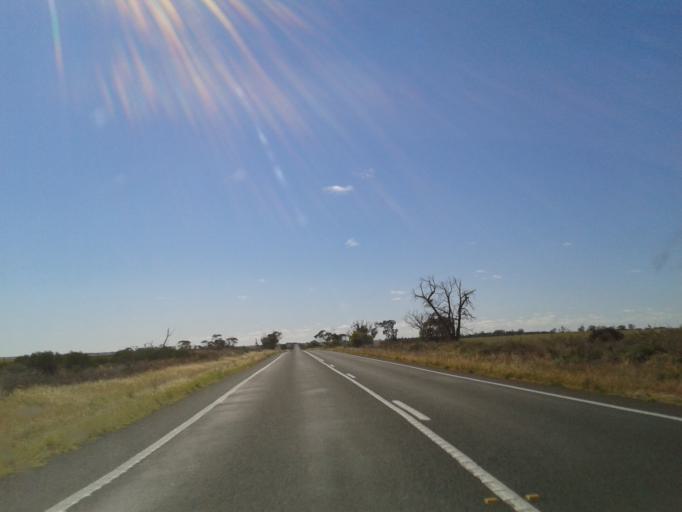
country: AU
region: New South Wales
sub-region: Wentworth
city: Dareton
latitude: -34.2761
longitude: 141.4155
